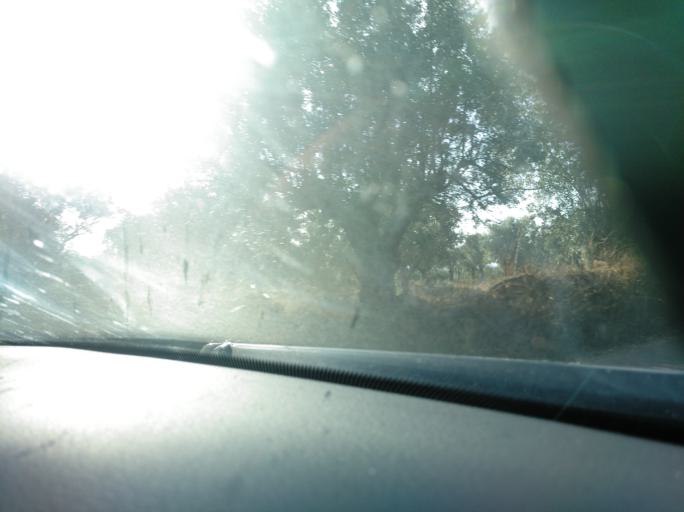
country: PT
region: Portalegre
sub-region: Elvas
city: Elvas
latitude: 38.8652
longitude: -7.2760
